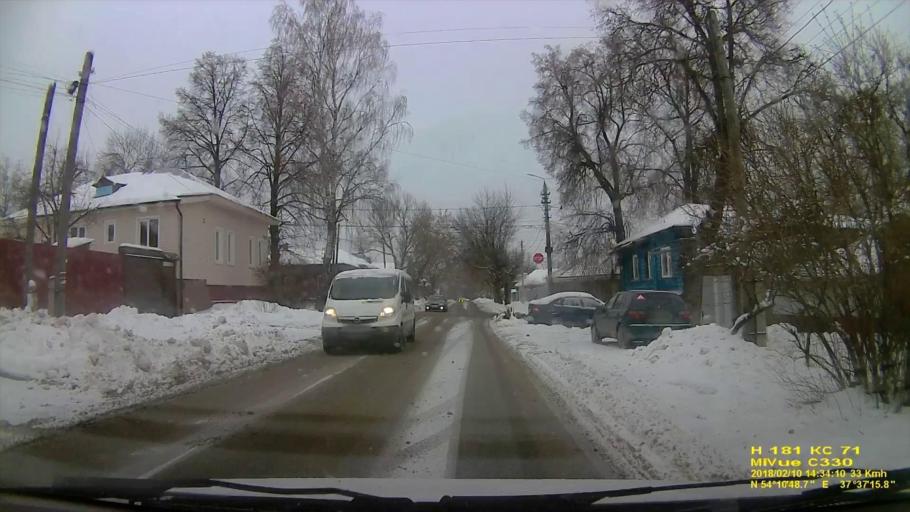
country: RU
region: Tula
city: Tula
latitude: 54.1802
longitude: 37.6210
